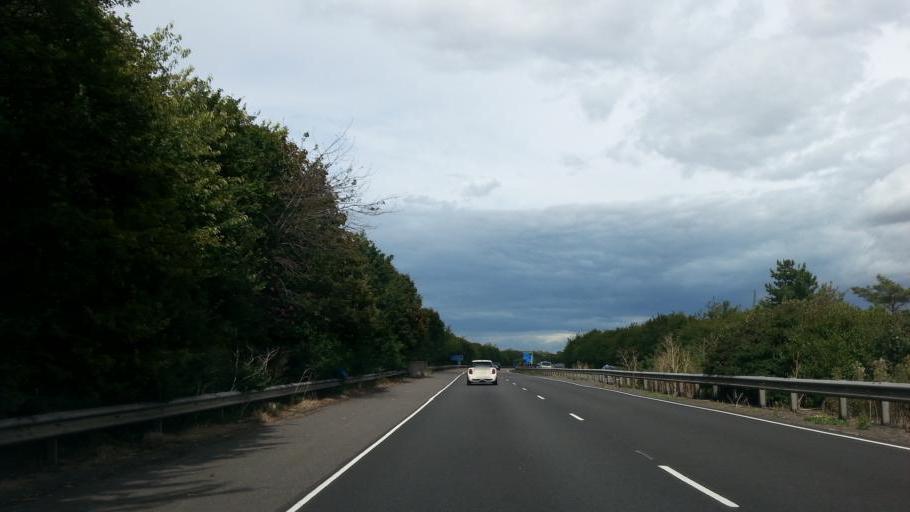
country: GB
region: England
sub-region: Cambridgeshire
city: Duxford
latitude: 52.0666
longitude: 0.1858
